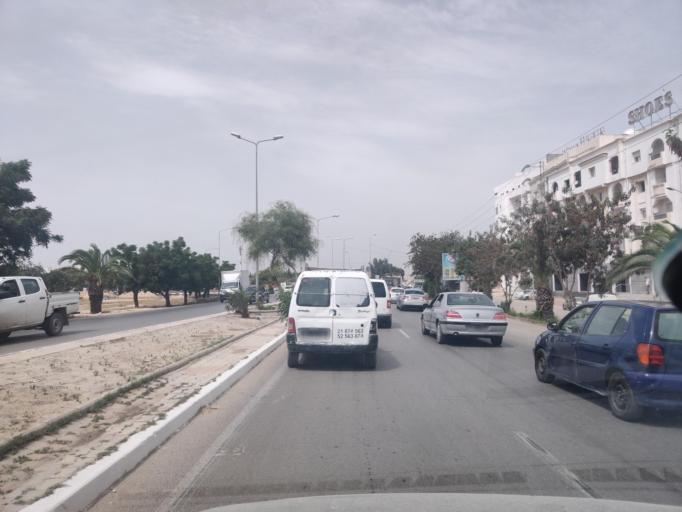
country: TN
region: Susah
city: Hammam Sousse
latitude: 35.8391
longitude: 10.5845
